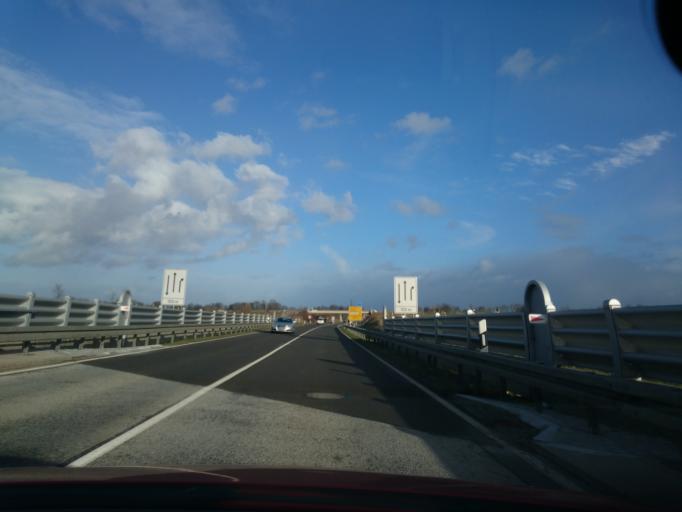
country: DE
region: Mecklenburg-Vorpommern
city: Stralsund
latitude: 54.2957
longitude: 13.0472
